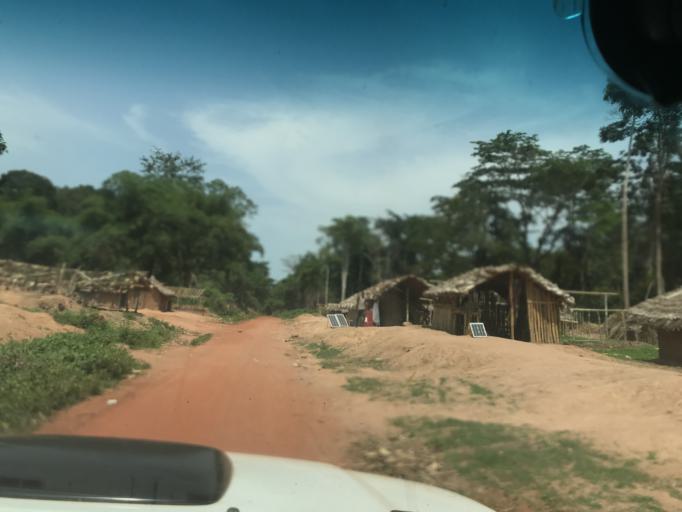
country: CD
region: Eastern Province
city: Aketi
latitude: 2.8876
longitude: 23.9823
